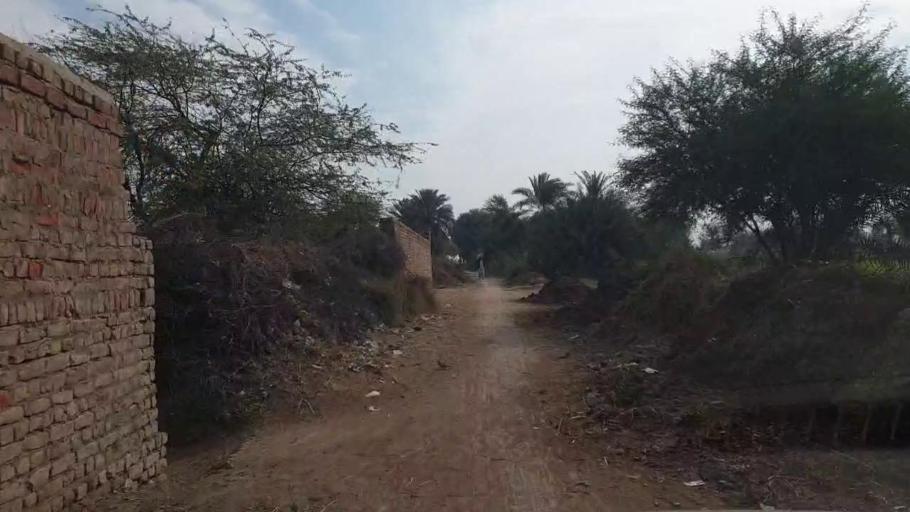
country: PK
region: Sindh
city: Shahdadpur
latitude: 25.9435
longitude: 68.6831
